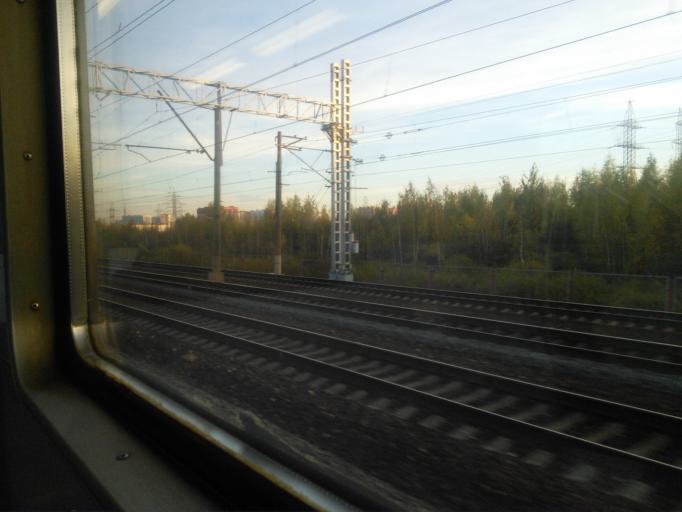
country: RU
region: Moskovskaya
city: Novopodrezkovo
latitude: 55.9305
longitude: 37.3668
